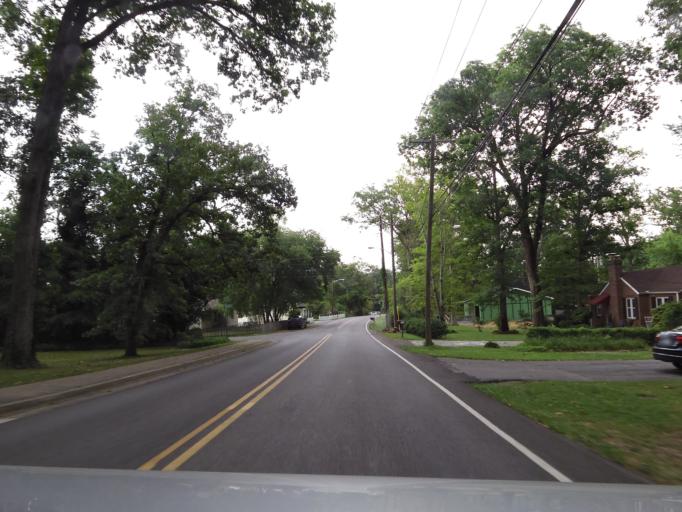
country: US
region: Tennessee
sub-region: Knox County
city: Knoxville
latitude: 35.9445
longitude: -83.9066
